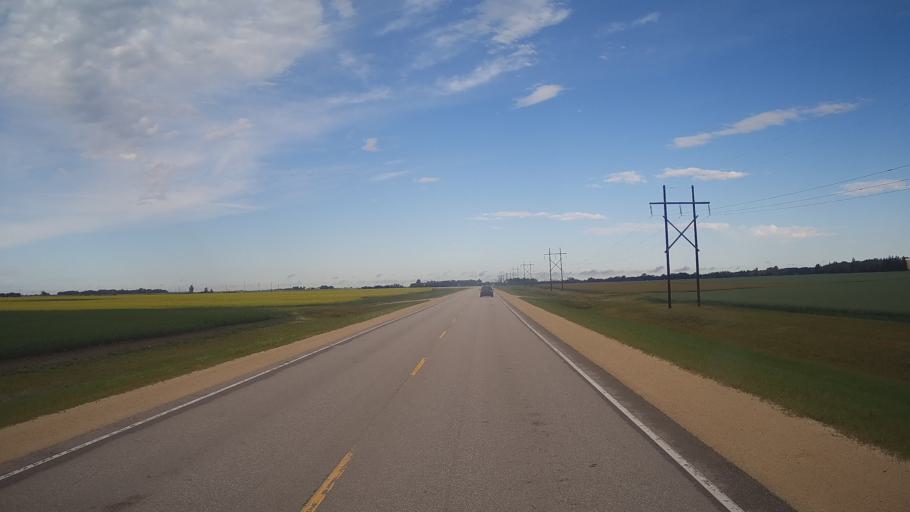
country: CA
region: Manitoba
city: Stonewall
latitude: 50.1228
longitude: -97.5149
